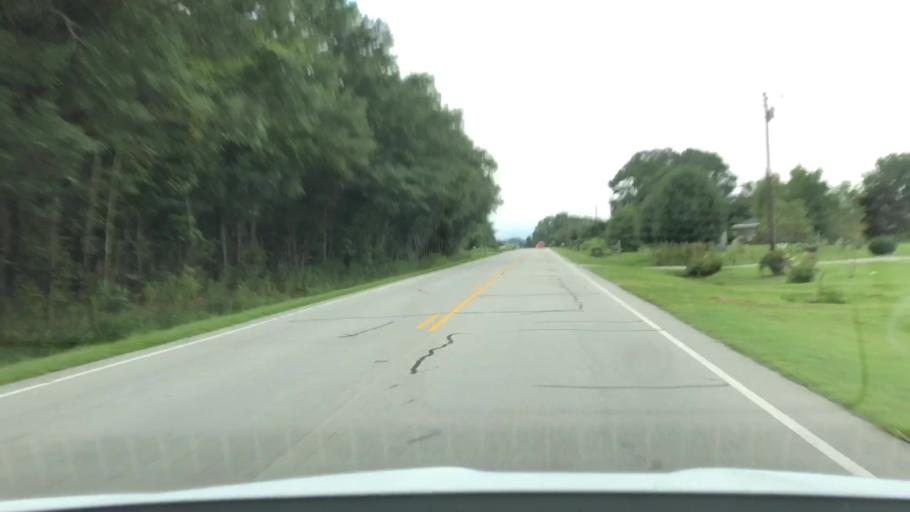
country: US
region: North Carolina
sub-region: Lenoir County
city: Kinston
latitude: 35.1340
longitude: -77.5264
